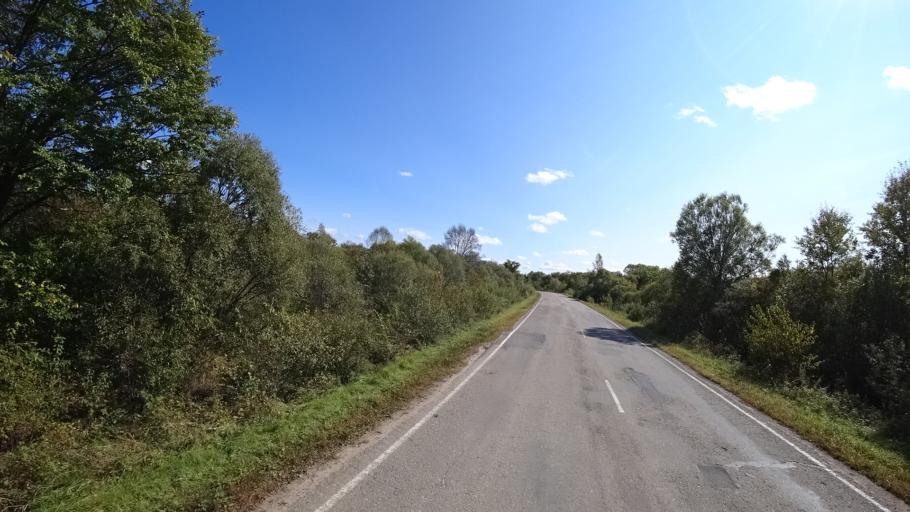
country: RU
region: Amur
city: Arkhara
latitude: 49.4024
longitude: 130.1292
